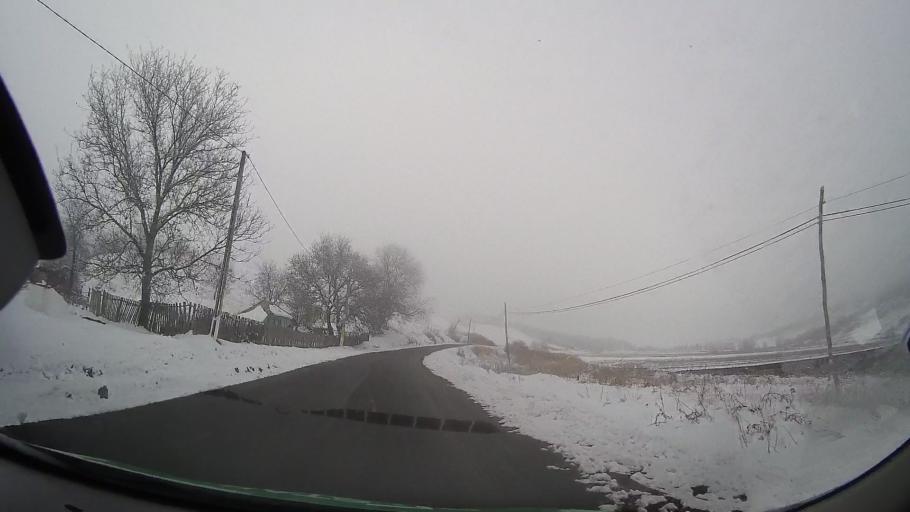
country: RO
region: Bacau
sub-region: Comuna Oncesti
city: Oncesti
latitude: 46.4832
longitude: 27.2565
